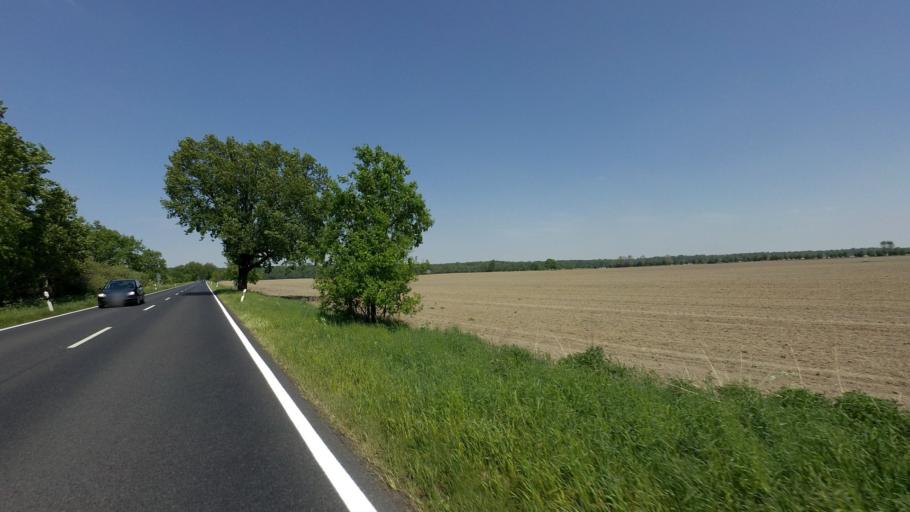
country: DE
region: Brandenburg
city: Gransee
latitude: 53.0497
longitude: 13.1946
